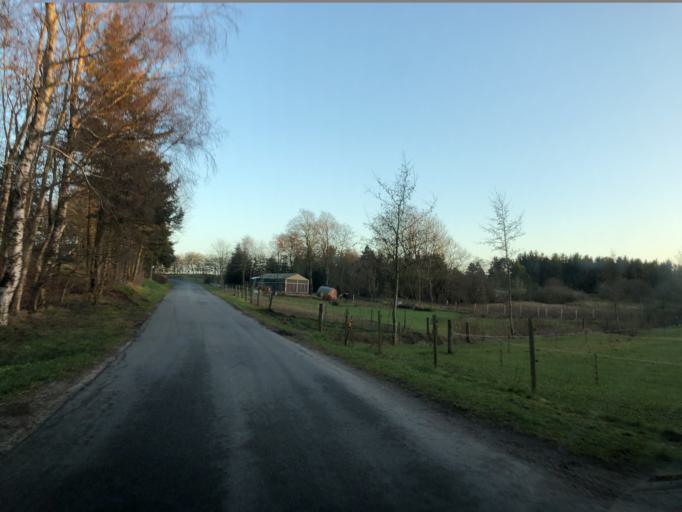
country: DK
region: Central Jutland
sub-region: Skive Kommune
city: Skive
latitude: 56.5439
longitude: 8.9274
